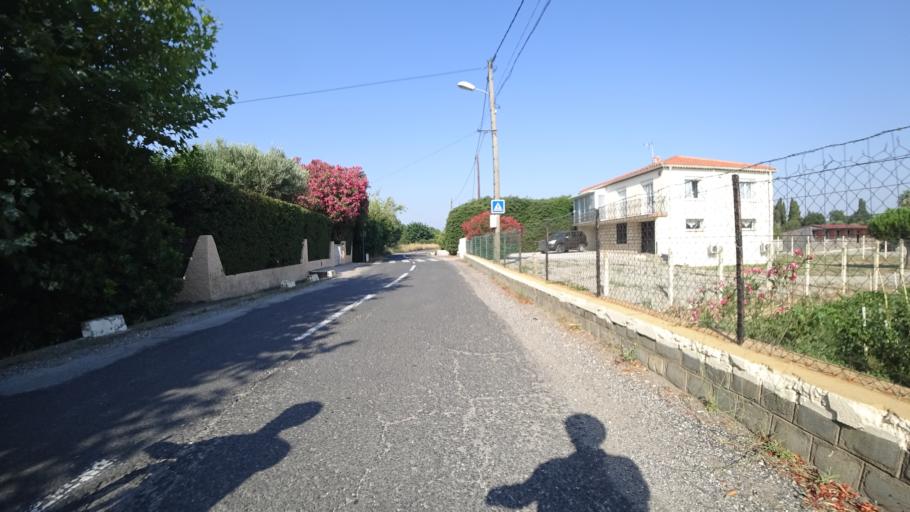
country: FR
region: Languedoc-Roussillon
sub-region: Departement des Pyrenees-Orientales
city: Perpignan
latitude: 42.7011
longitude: 2.8759
